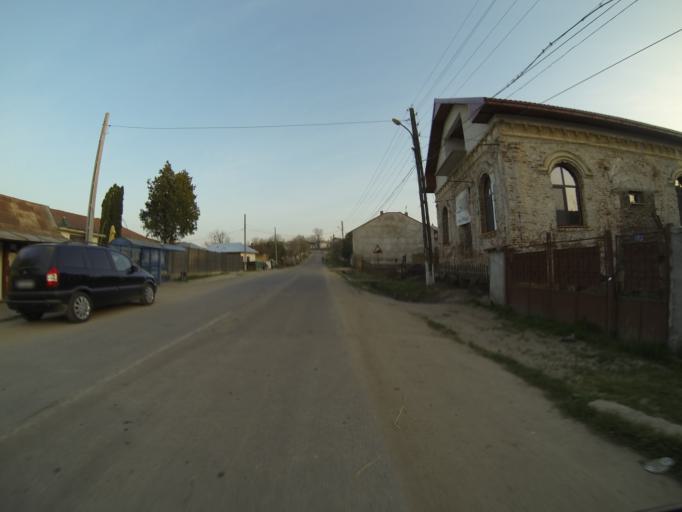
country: RO
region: Dolj
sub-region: Comuna Dranicu
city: Dranic
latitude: 44.0547
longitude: 23.8457
